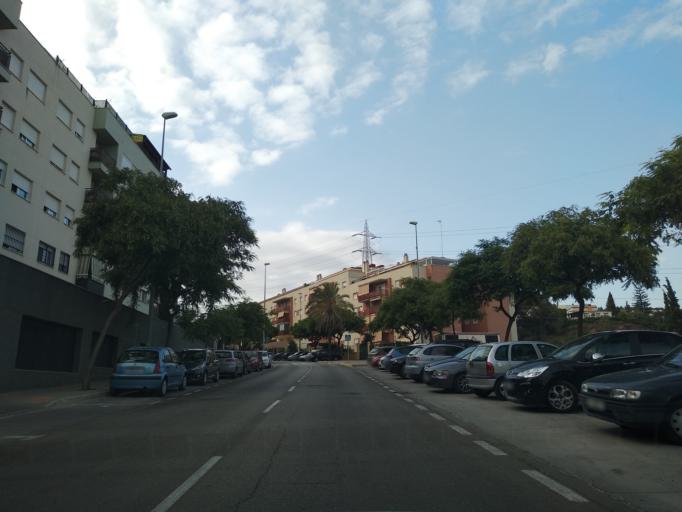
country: ES
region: Andalusia
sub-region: Provincia de Malaga
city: Malaga
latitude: 36.7310
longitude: -4.4747
